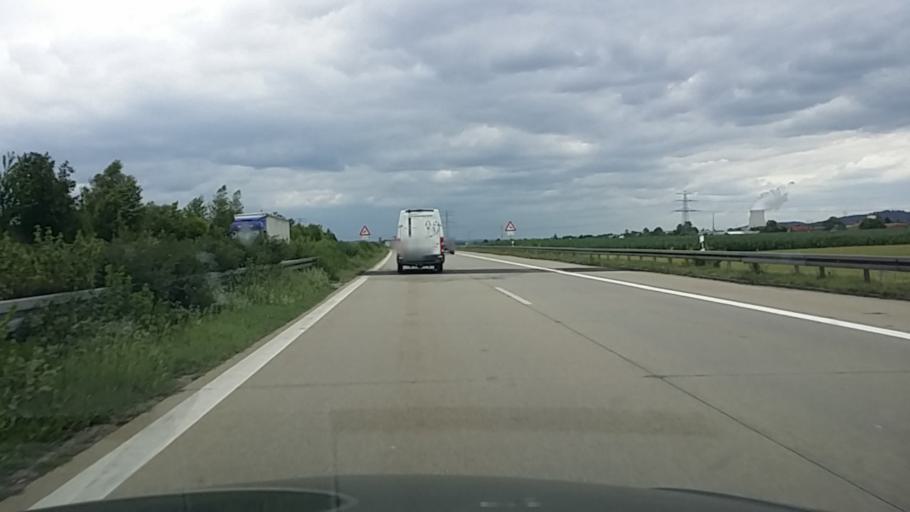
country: DE
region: Bavaria
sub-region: Lower Bavaria
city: Essenbach
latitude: 48.5935
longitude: 12.2167
